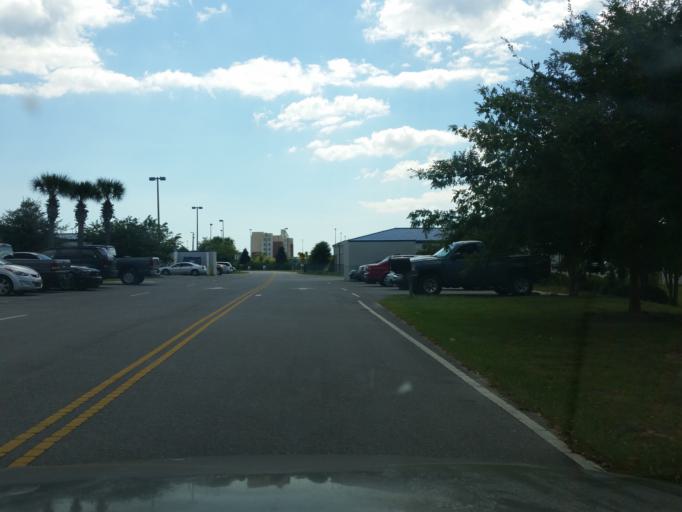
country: US
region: Florida
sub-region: Escambia County
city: Ferry Pass
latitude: 30.4801
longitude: -87.1949
